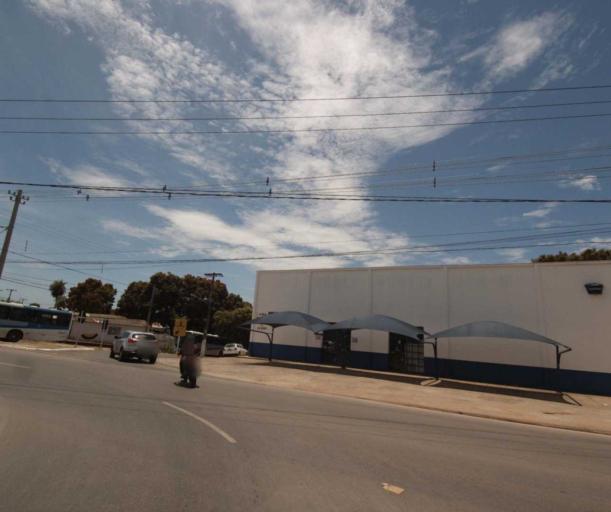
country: BR
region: Mato Grosso
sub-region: Varzea Grande
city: Varzea Grande
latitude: -15.6139
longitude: -56.1261
